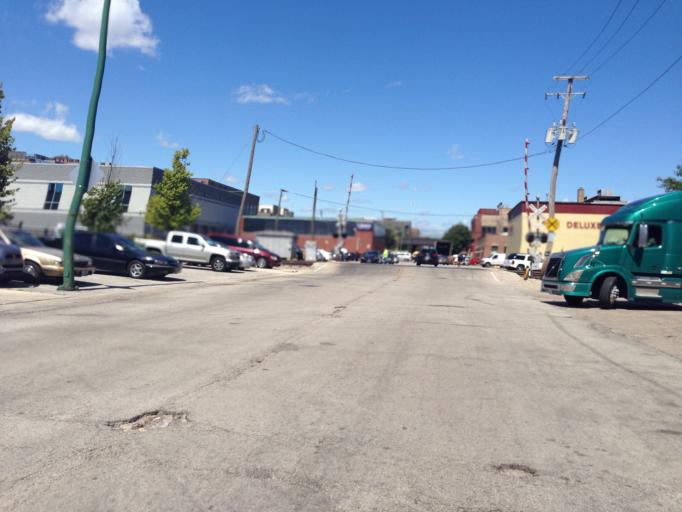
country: US
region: Illinois
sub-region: Cook County
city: Chicago
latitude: 41.8880
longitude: -87.6533
